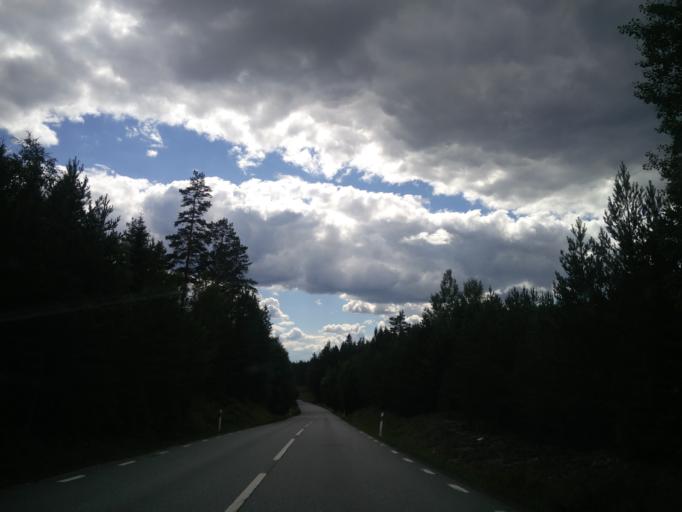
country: SE
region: OErebro
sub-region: Ljusnarsbergs Kommun
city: Kopparberg
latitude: 59.8936
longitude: 15.0157
